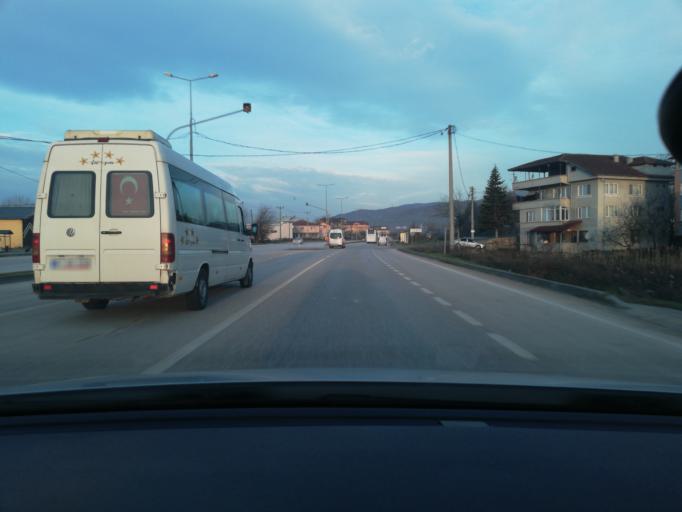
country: TR
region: Duzce
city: Konuralp
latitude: 40.9005
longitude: 31.1520
